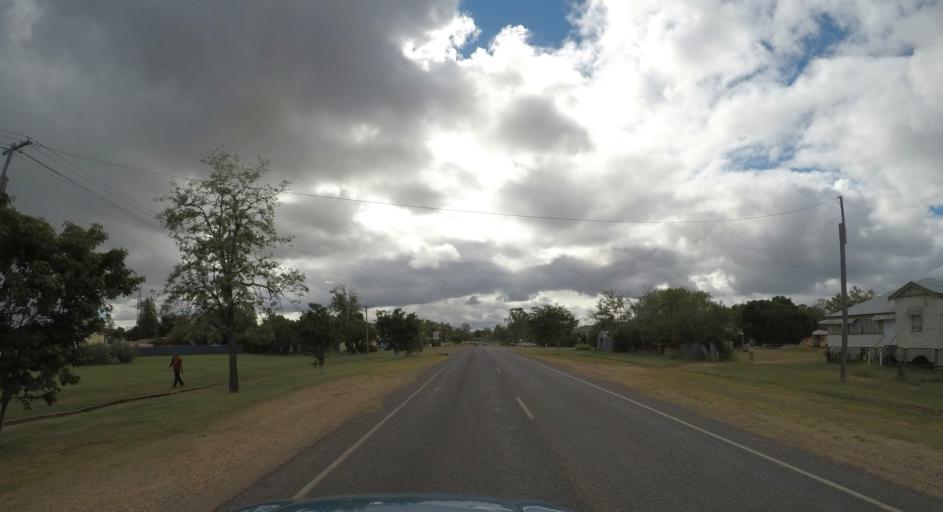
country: AU
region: Queensland
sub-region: North Burnett
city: Gayndah
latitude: -25.5891
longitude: 151.3016
